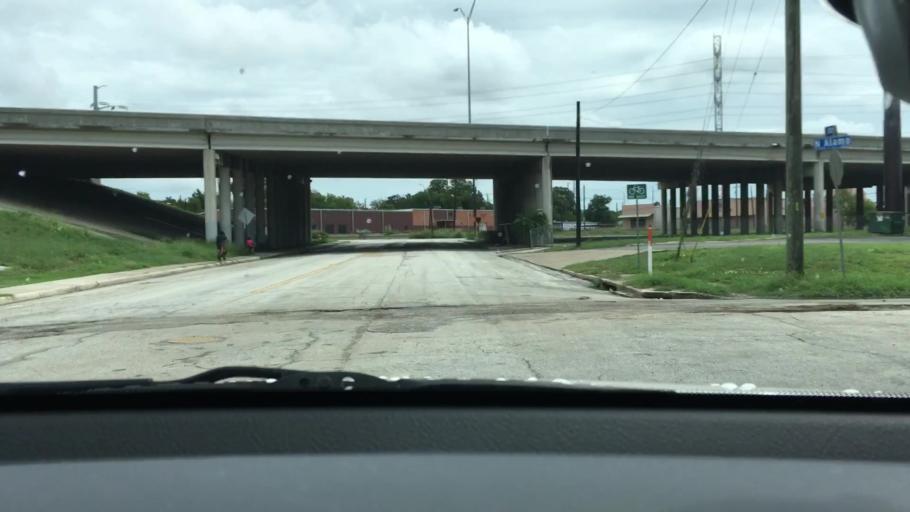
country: US
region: Texas
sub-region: Bexar County
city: San Antonio
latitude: 29.4346
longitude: -98.4788
